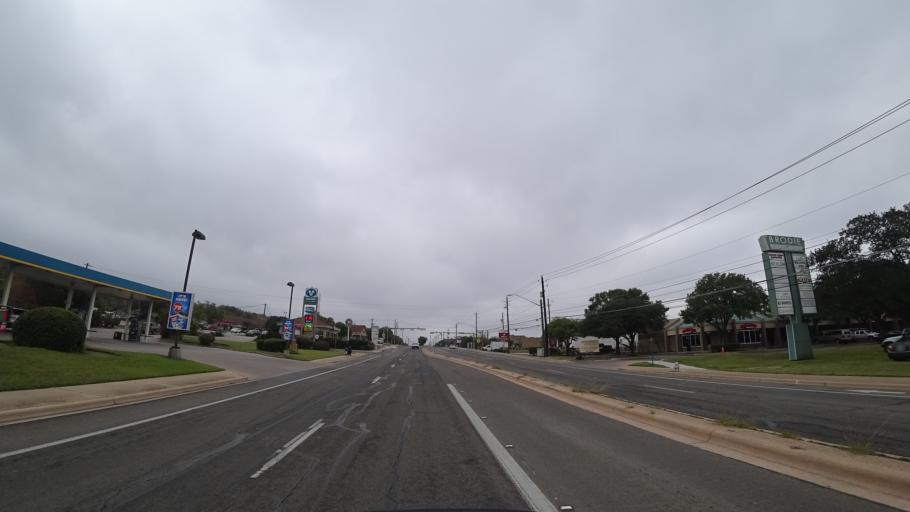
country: US
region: Texas
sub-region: Travis County
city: Shady Hollow
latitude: 30.2018
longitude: -97.8381
